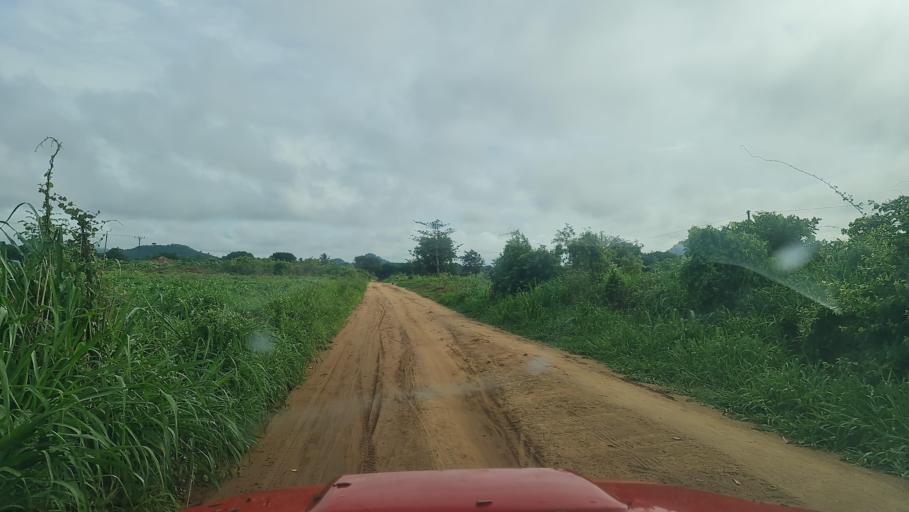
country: MW
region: Southern Region
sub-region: Nsanje District
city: Nsanje
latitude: -17.2821
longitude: 35.6138
